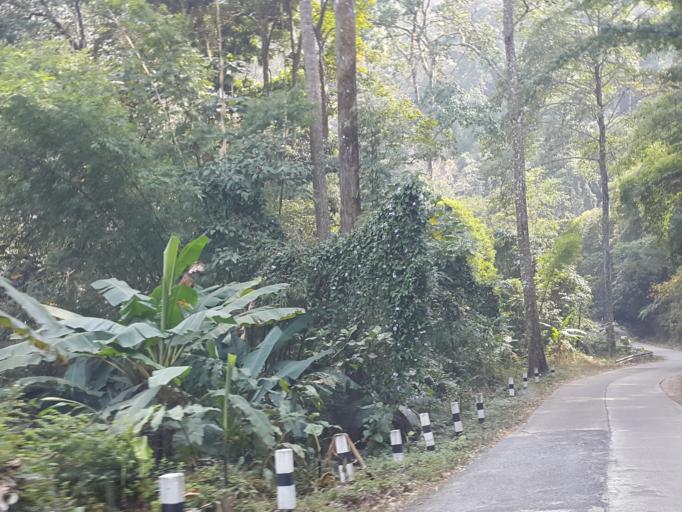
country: TH
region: Chiang Mai
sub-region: Amphoe Chiang Dao
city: Chiang Dao
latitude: 19.4111
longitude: 98.8708
